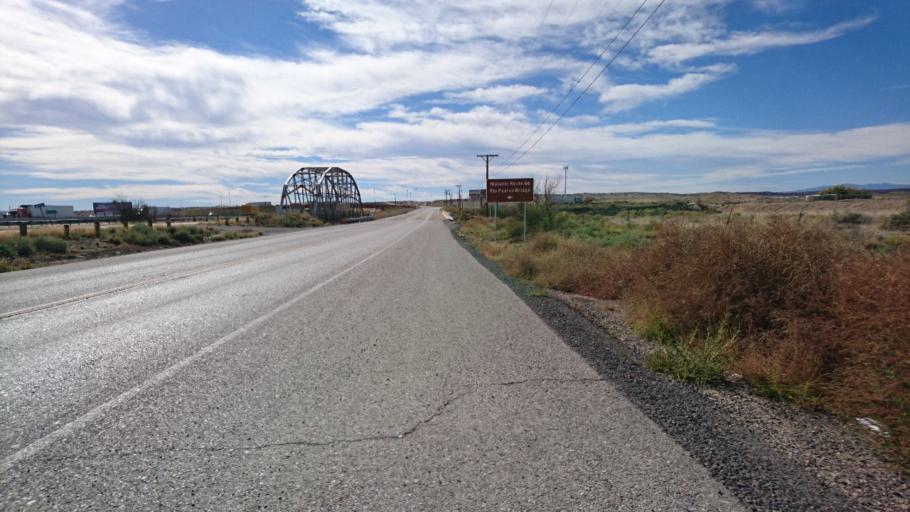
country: US
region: New Mexico
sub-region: Bernalillo County
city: South Valley
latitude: 35.0341
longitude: -106.9405
